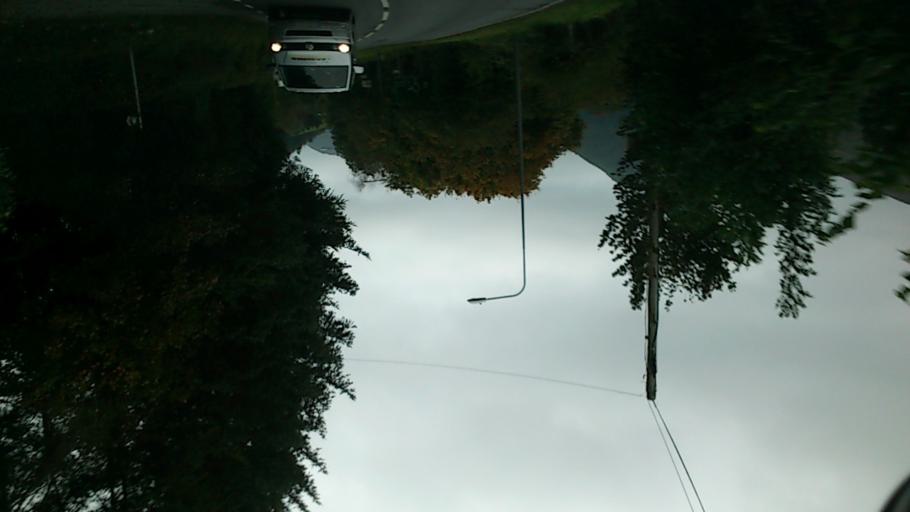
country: GB
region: Wales
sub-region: Gwynedd
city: Corris
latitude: 52.6964
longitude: -3.6842
